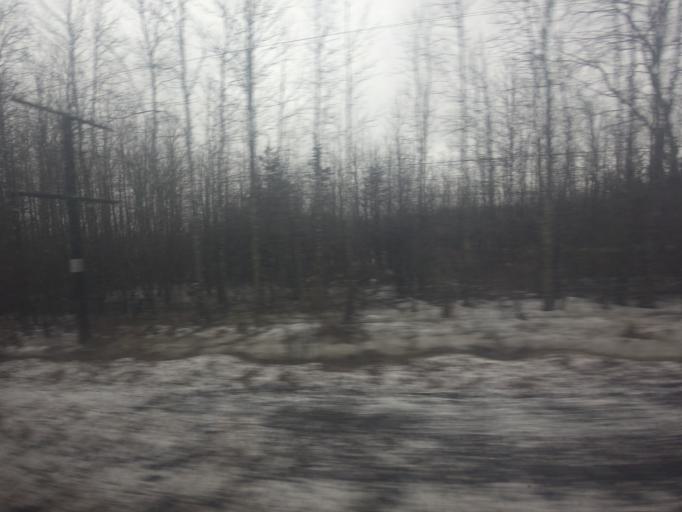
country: CA
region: Ontario
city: Deseronto
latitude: 44.2252
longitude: -77.1190
